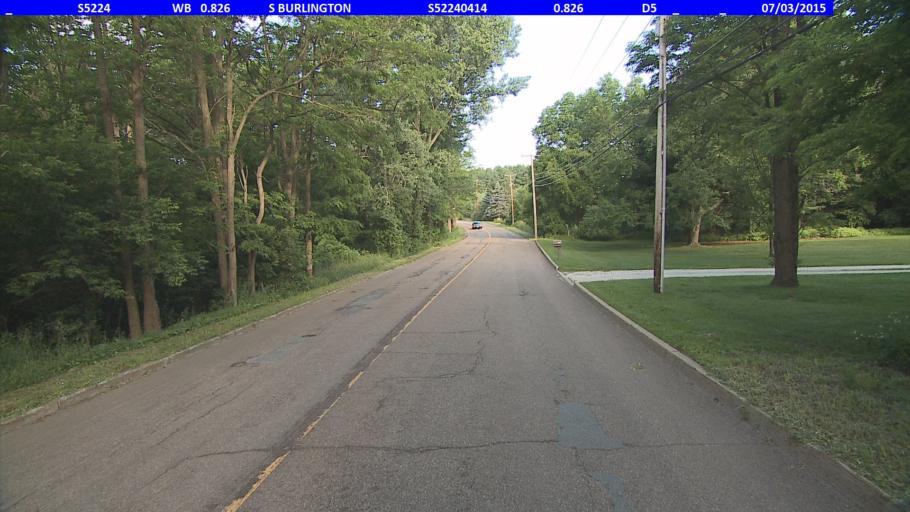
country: US
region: Vermont
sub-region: Chittenden County
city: South Burlington
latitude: 44.4445
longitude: -73.1927
